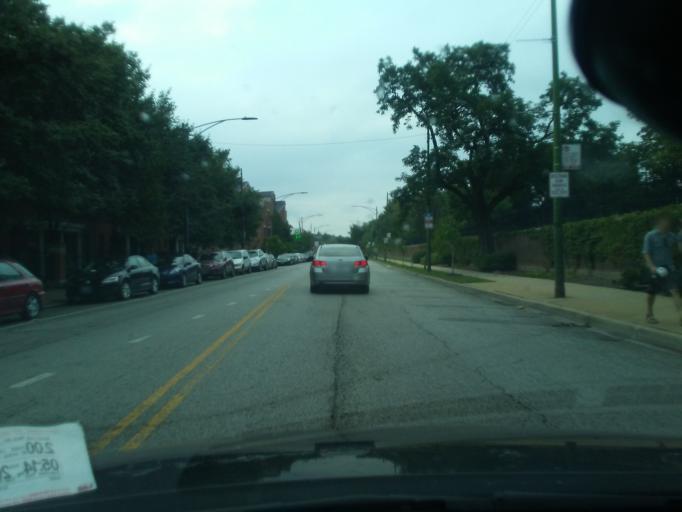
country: US
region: Illinois
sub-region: Cook County
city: Lincolnwood
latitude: 41.9549
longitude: -87.6626
